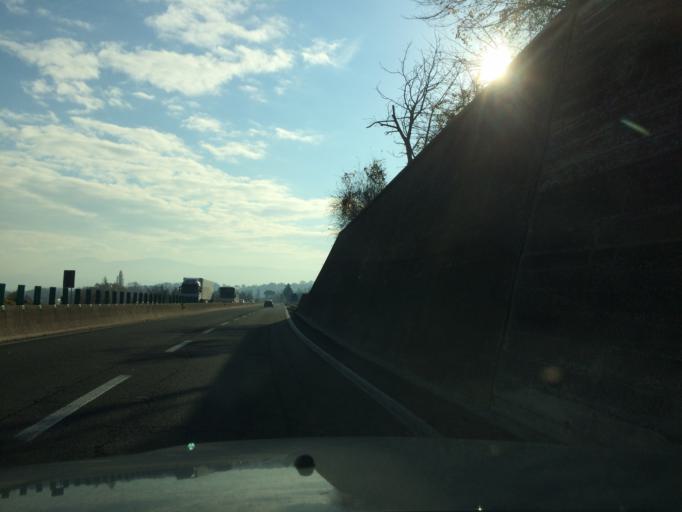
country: IT
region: Umbria
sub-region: Provincia di Terni
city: San Gemini
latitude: 42.5993
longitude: 12.5632
